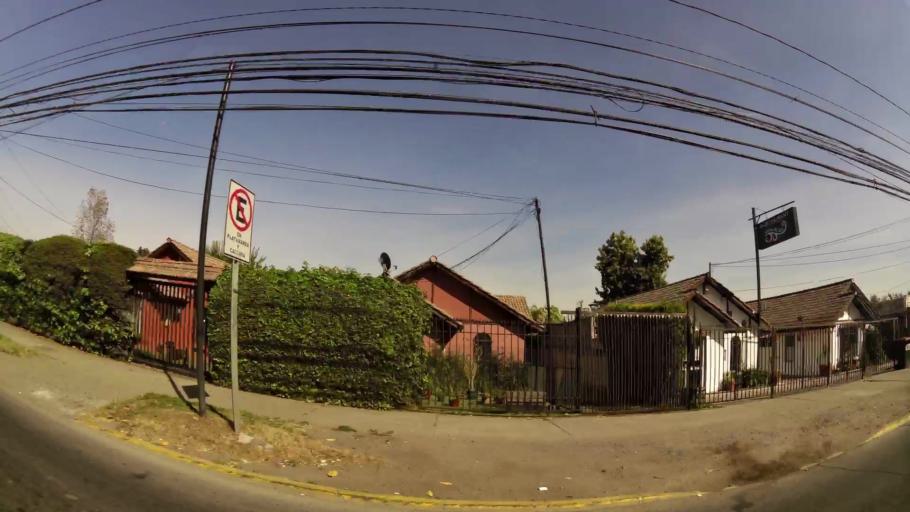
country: CL
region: Santiago Metropolitan
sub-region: Provincia de Santiago
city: Villa Presidente Frei, Nunoa, Santiago, Chile
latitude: -33.5002
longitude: -70.5609
